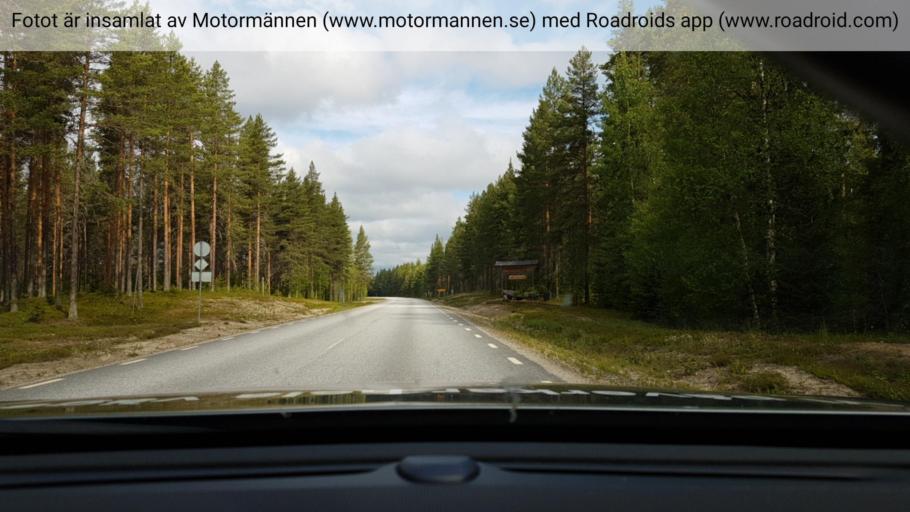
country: SE
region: Vaesterbotten
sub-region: Vindelns Kommun
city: Vindeln
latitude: 64.3681
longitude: 19.4291
